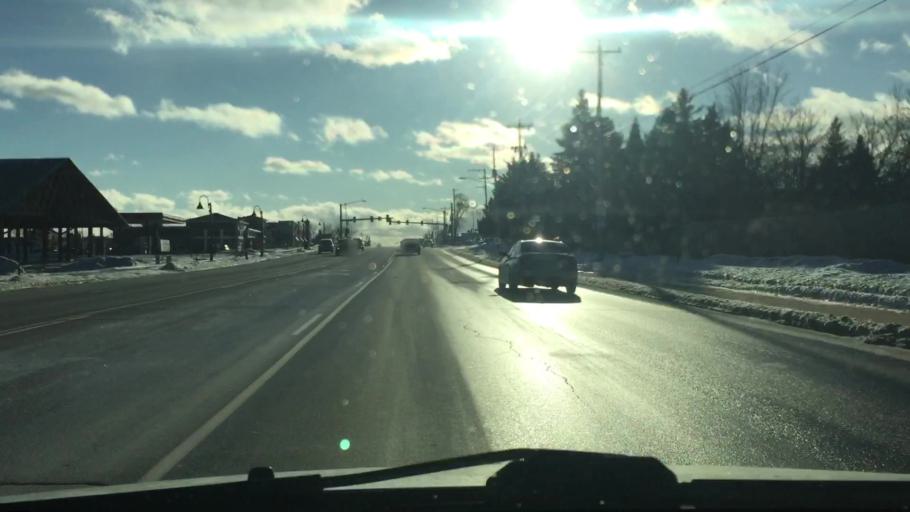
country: US
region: Wisconsin
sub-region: Waukesha County
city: New Berlin
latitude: 42.9819
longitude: -88.1009
